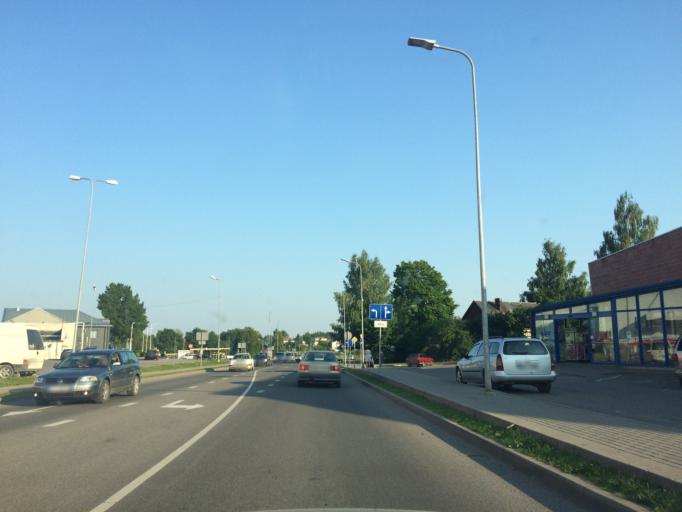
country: LV
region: Rezekne
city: Rezekne
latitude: 56.5173
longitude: 27.3499
